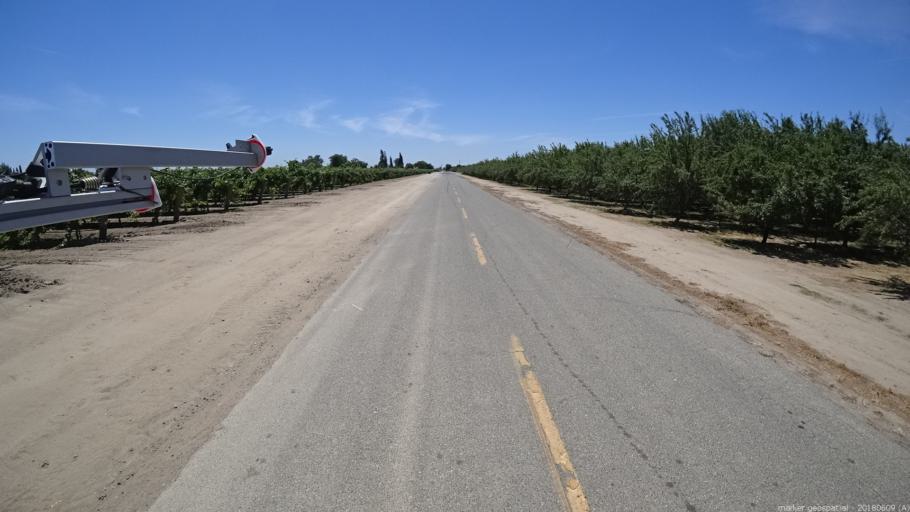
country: US
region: California
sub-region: Madera County
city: Parkwood
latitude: 36.9126
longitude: -120.0742
